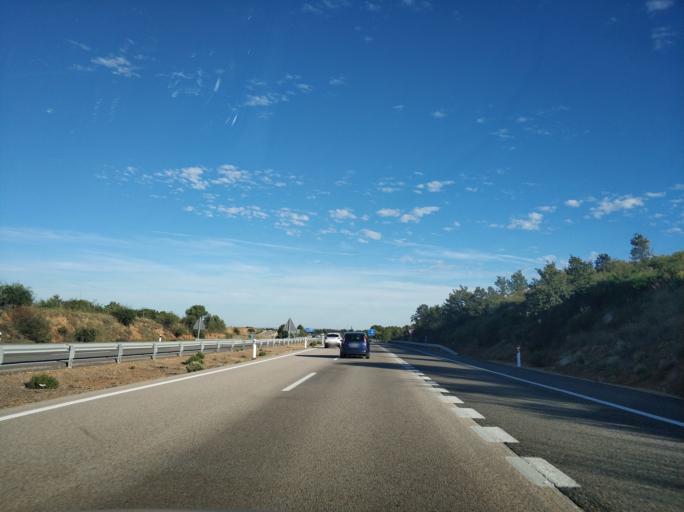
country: ES
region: Castille and Leon
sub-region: Provincia de Leon
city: Valverde de la Virgen
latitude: 42.5877
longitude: -5.6818
